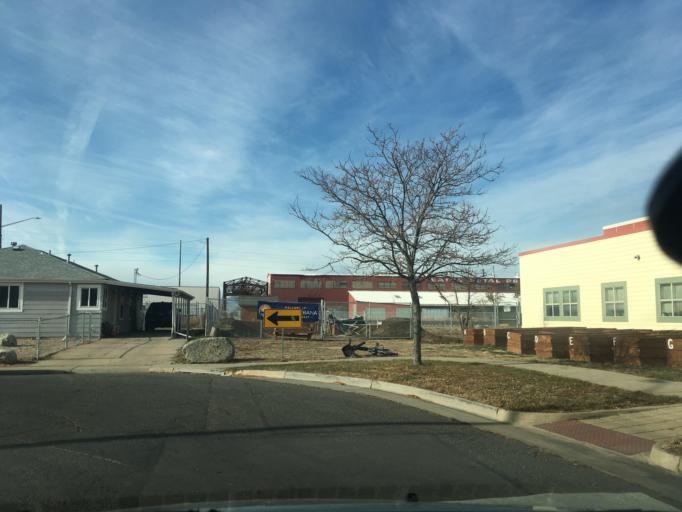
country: US
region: Colorado
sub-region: Adams County
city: Commerce City
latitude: 39.7838
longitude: -104.9569
